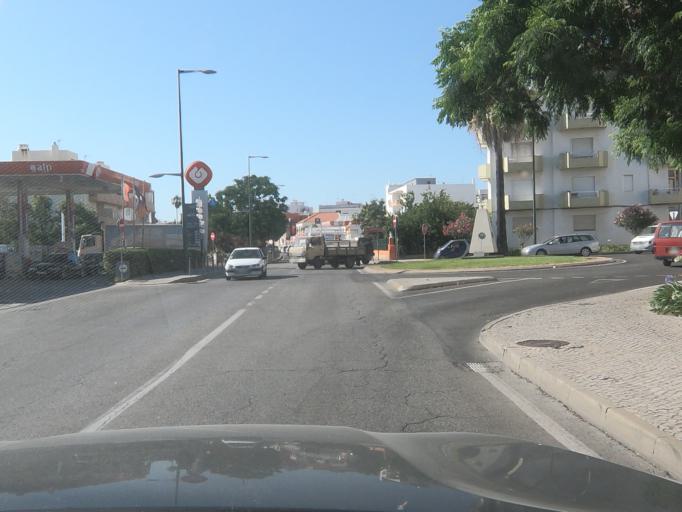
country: PT
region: Faro
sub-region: Loule
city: Loule
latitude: 37.1340
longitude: -8.0205
